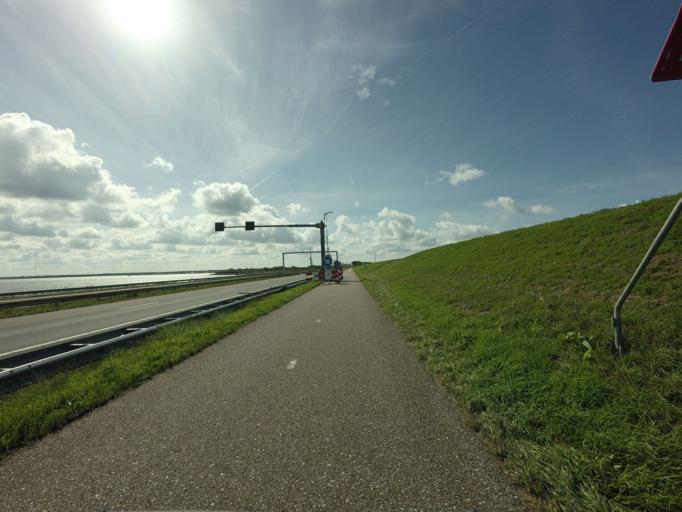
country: NL
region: North Holland
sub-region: Gemeente Hollands Kroon
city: Den Oever
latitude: 52.9424
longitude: 5.0575
